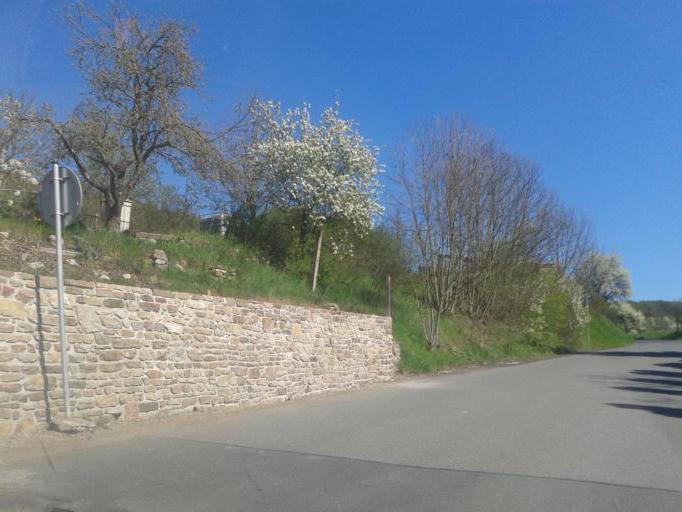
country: CZ
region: Central Bohemia
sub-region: Okres Beroun
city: Beroun
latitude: 49.9289
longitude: 14.0663
